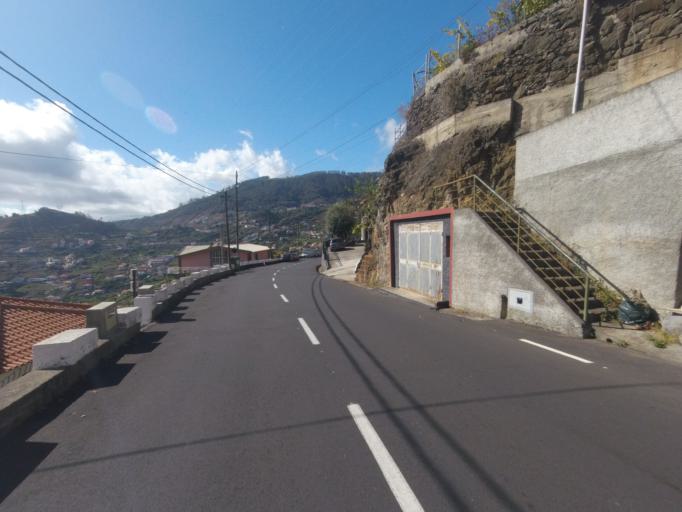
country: PT
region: Madeira
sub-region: Ribeira Brava
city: Campanario
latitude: 32.6692
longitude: -17.0207
